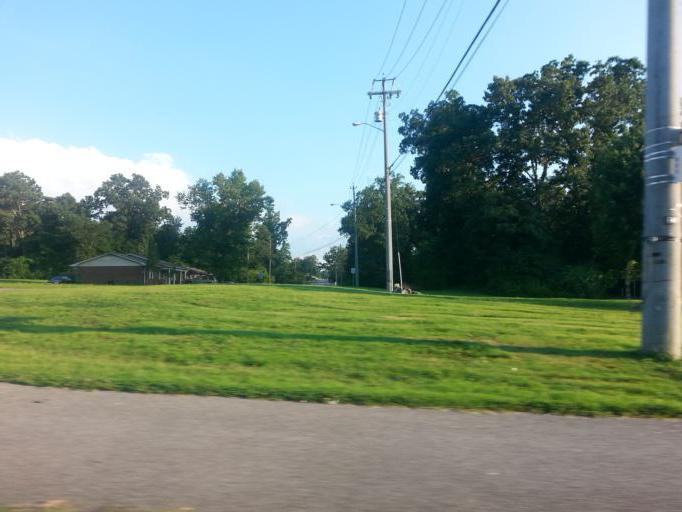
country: US
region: Tennessee
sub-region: Knox County
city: Knoxville
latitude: 35.9866
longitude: -83.9914
